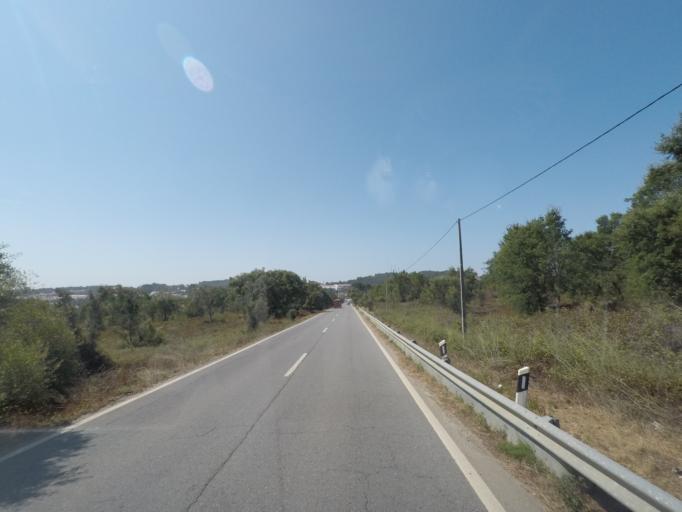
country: PT
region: Beja
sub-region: Odemira
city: Sao Teotonio
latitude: 37.5202
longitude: -8.7038
